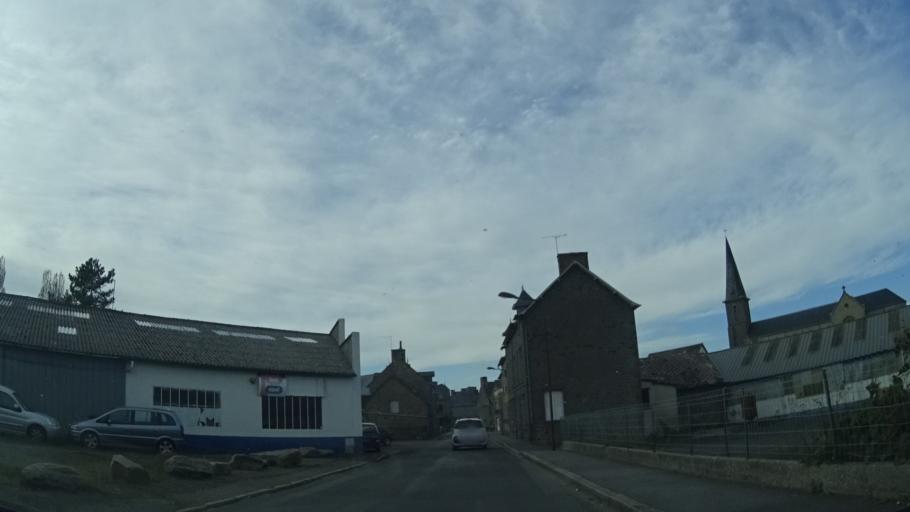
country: FR
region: Brittany
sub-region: Departement d'Ille-et-Vilaine
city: Bonnemain
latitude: 48.4664
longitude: -1.7645
